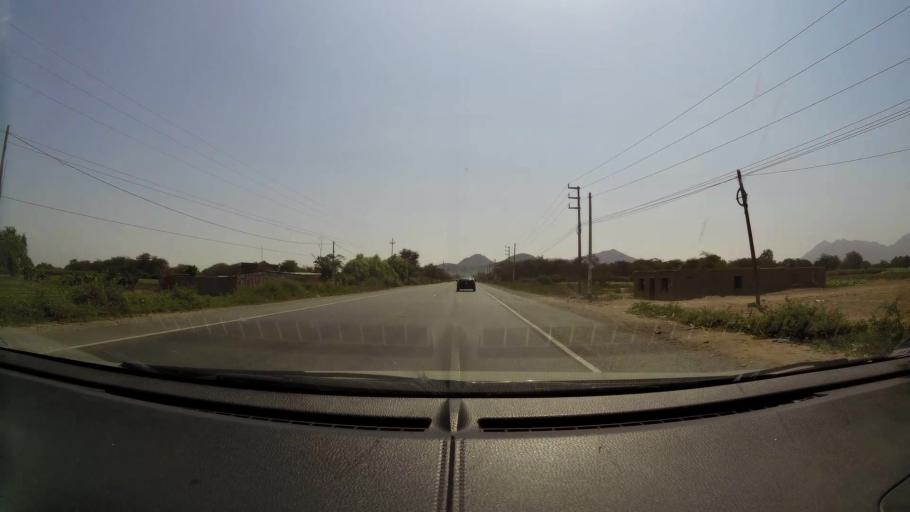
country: PE
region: Lambayeque
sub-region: Provincia de Chiclayo
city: Mocupe
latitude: -6.9832
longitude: -79.6359
